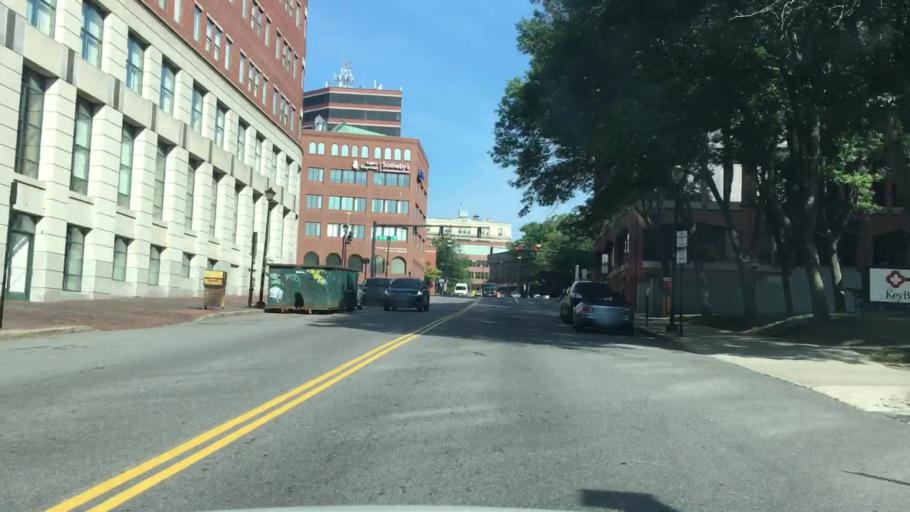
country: US
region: Maine
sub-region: Cumberland County
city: Portland
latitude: 43.6562
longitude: -70.2555
